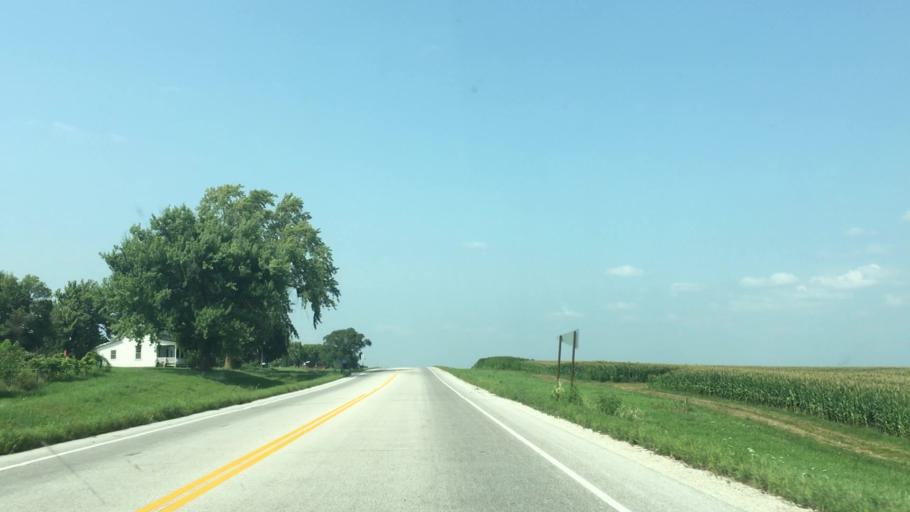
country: US
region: Minnesota
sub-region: Fillmore County
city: Harmony
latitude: 43.5367
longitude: -91.9296
